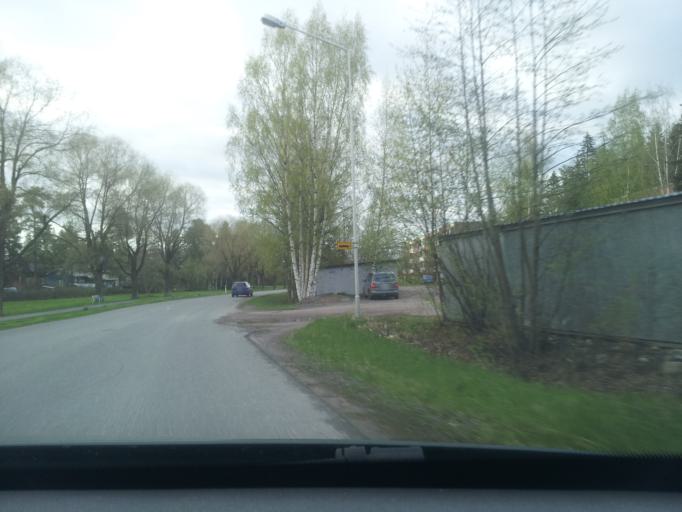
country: FI
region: Haeme
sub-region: Riihimaeki
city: Riihimaeki
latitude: 60.7489
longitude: 24.7670
